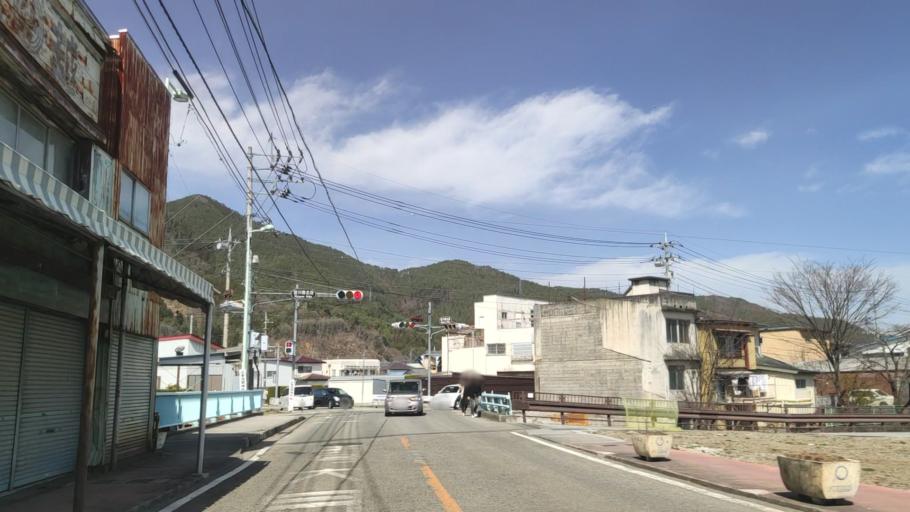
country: JP
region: Yamanashi
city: Fujikawaguchiko
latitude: 35.4945
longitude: 138.8044
